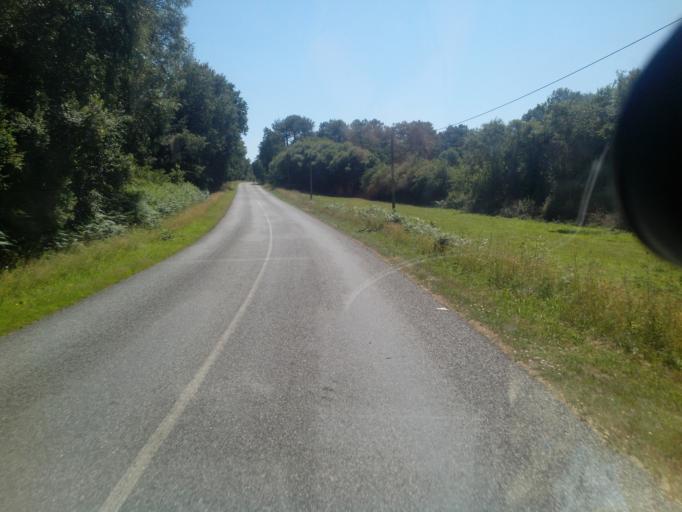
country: FR
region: Brittany
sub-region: Departement du Morbihan
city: Campeneac
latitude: 47.9969
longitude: -2.2503
